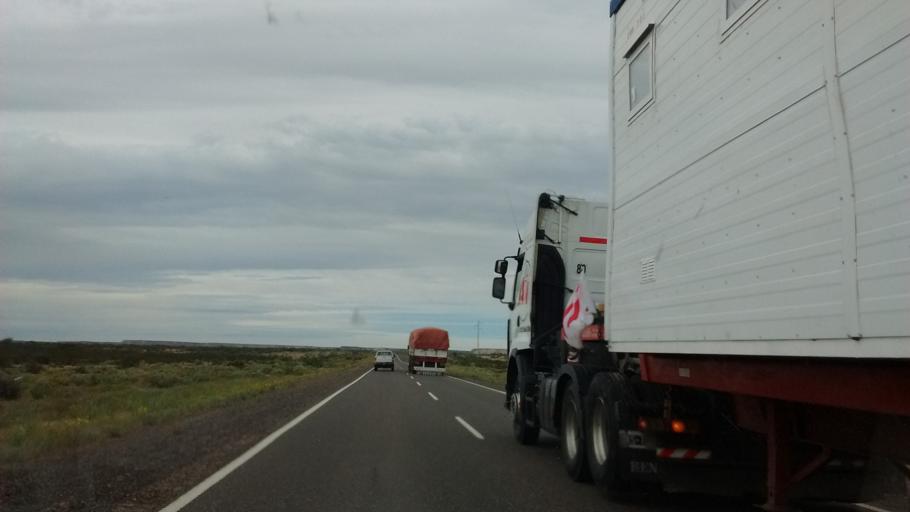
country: AR
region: Rio Negro
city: Catriel
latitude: -38.1392
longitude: -67.9383
